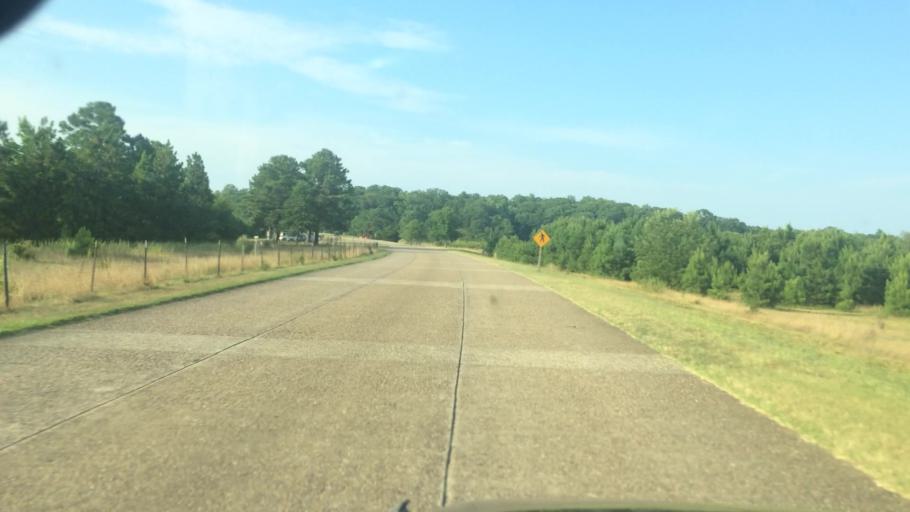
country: US
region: Virginia
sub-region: City of Williamsburg
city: Williamsburg
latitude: 37.2222
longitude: -76.6966
